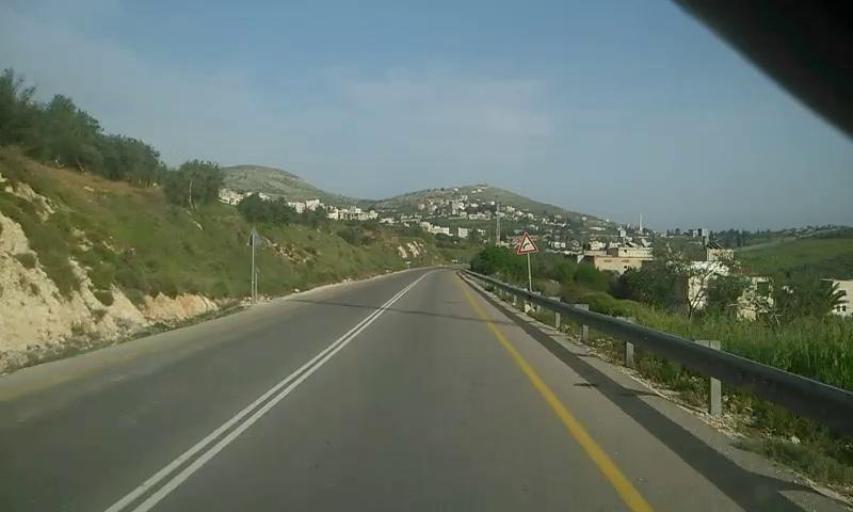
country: PS
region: West Bank
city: Madama
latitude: 32.1841
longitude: 35.2383
